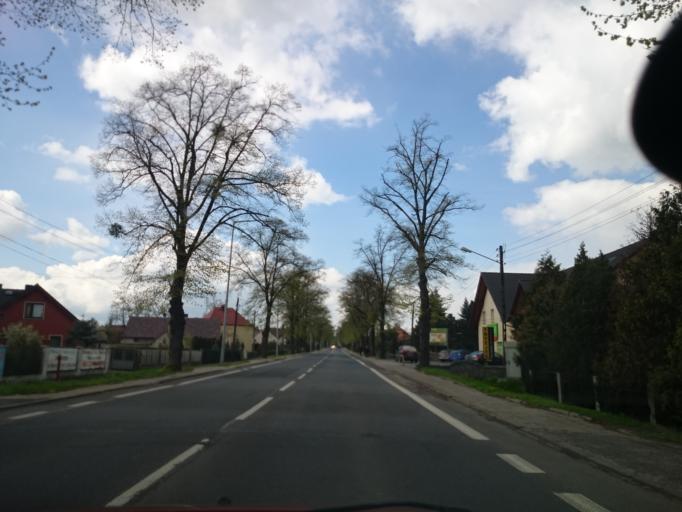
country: PL
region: Opole Voivodeship
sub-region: Powiat opolski
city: Opole
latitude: 50.6455
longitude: 17.9854
